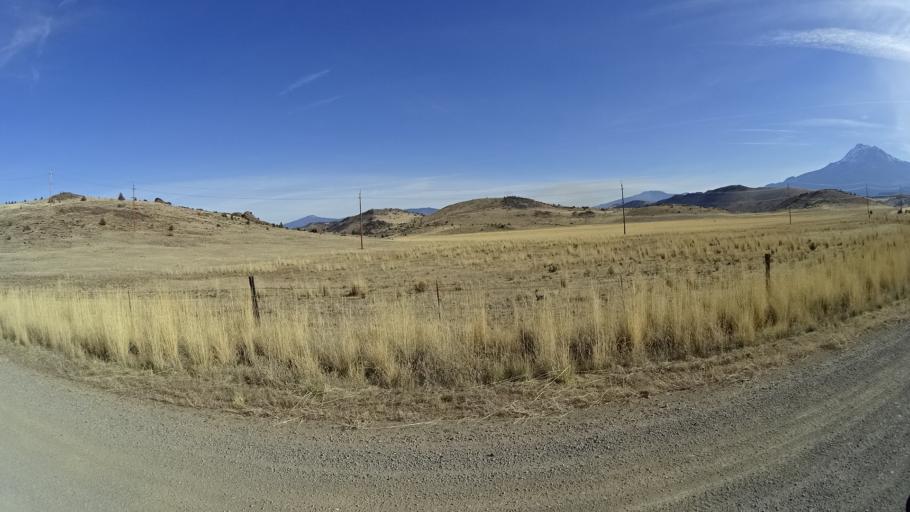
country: US
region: California
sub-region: Siskiyou County
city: Weed
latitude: 41.5129
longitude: -122.4702
